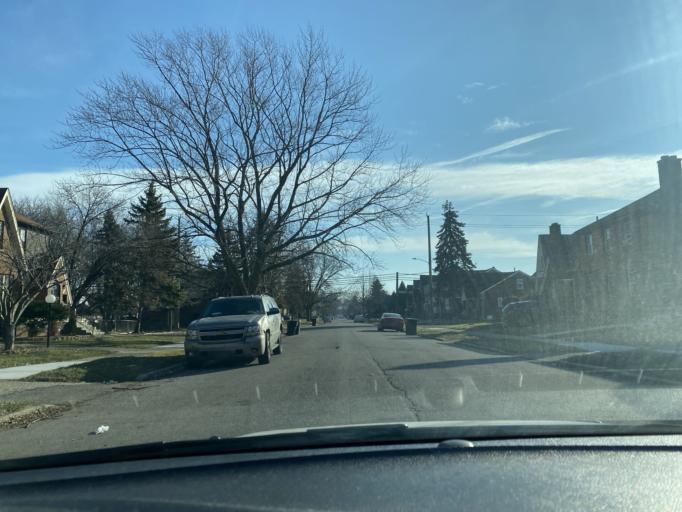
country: US
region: Michigan
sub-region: Wayne County
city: Grosse Pointe Park
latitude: 42.4083
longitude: -82.9475
